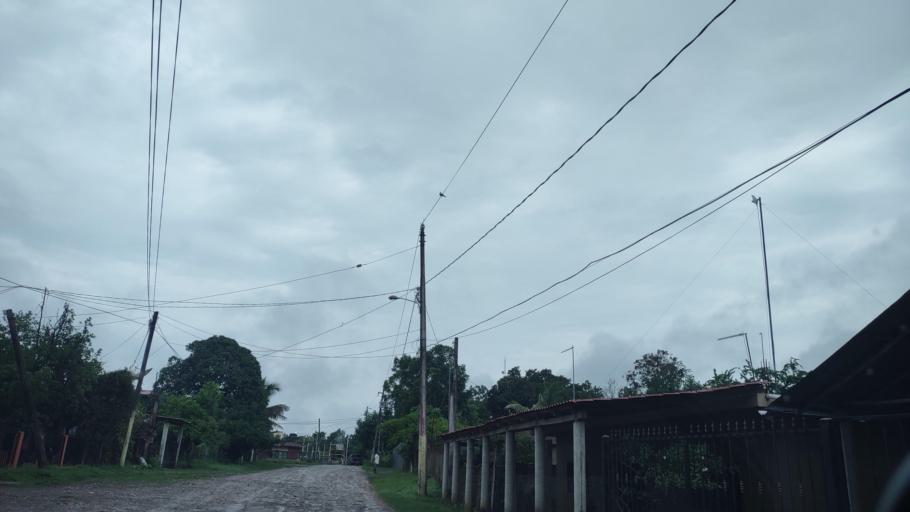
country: MX
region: San Luis Potosi
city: Tanquian de Escobedo
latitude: 21.5442
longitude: -98.5528
